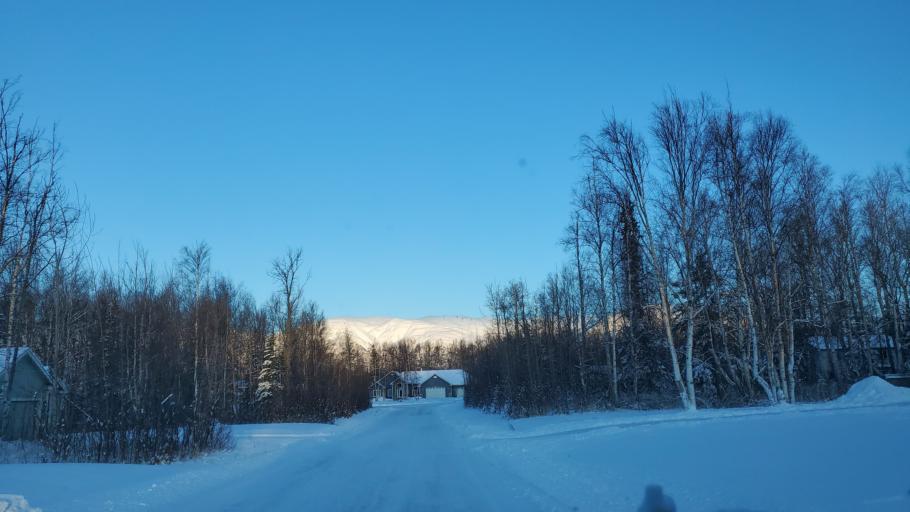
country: US
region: Alaska
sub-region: Matanuska-Susitna Borough
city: Lakes
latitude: 61.6378
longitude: -149.3093
